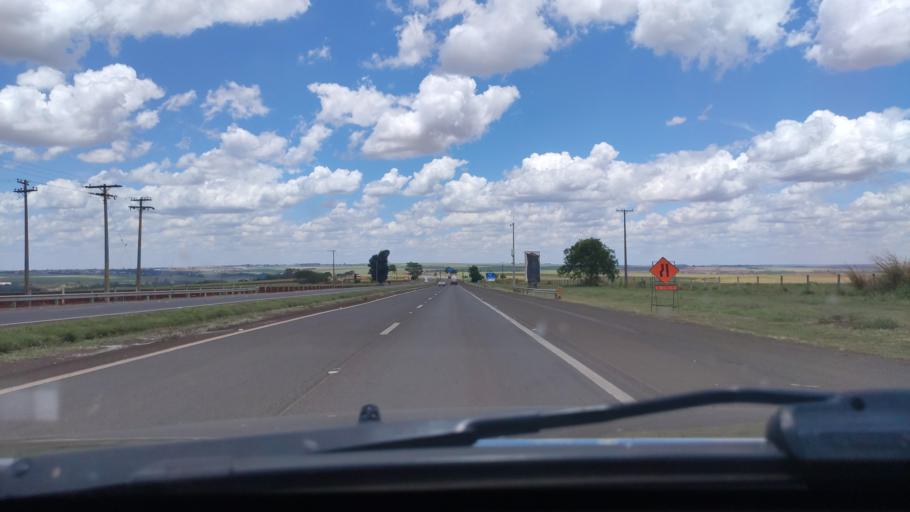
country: BR
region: Sao Paulo
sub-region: Itapui
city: Itapui
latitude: -22.3100
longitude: -48.7025
